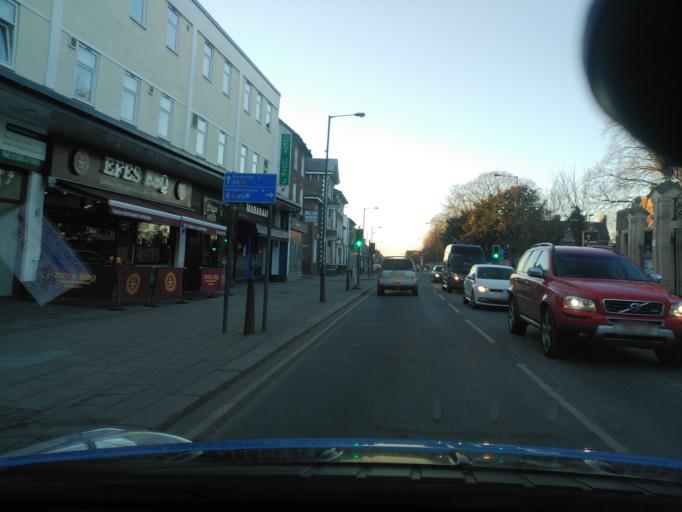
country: GB
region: England
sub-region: Central Bedfordshire
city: Dunstable
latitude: 51.8883
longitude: -0.5241
